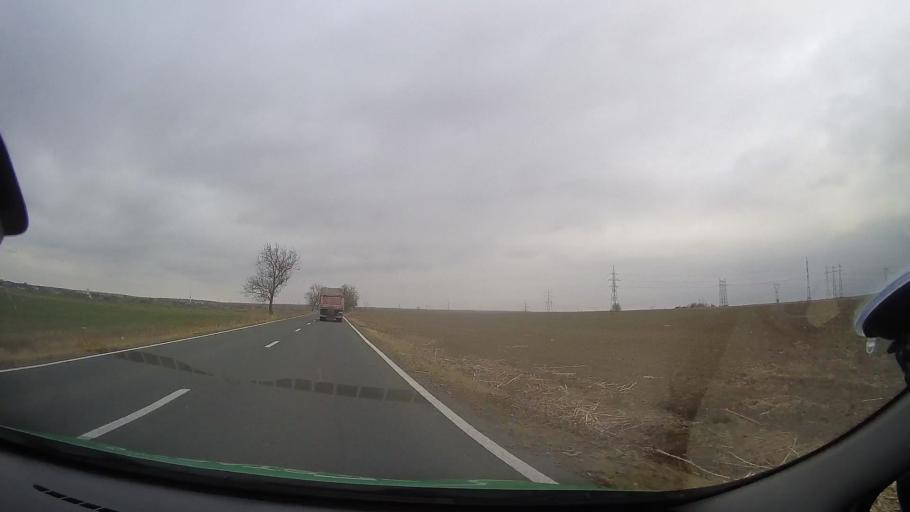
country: RO
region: Constanta
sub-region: Comuna Castelu
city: Castelu
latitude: 44.2551
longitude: 28.3518
